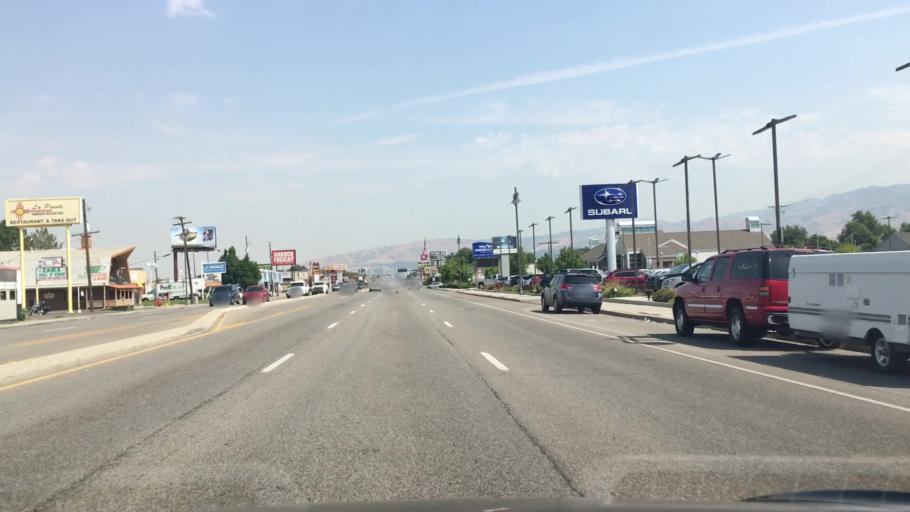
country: US
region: Utah
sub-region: Salt Lake County
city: Centerfield
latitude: 40.6935
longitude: -111.8882
